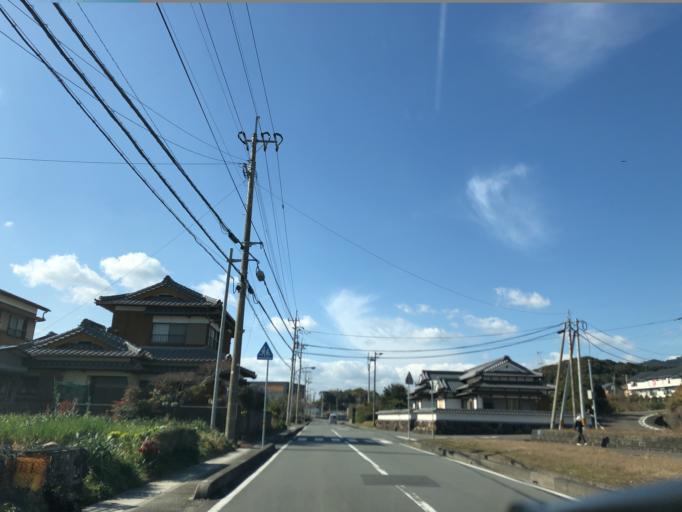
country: JP
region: Kochi
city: Sukumo
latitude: 32.9275
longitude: 132.6850
